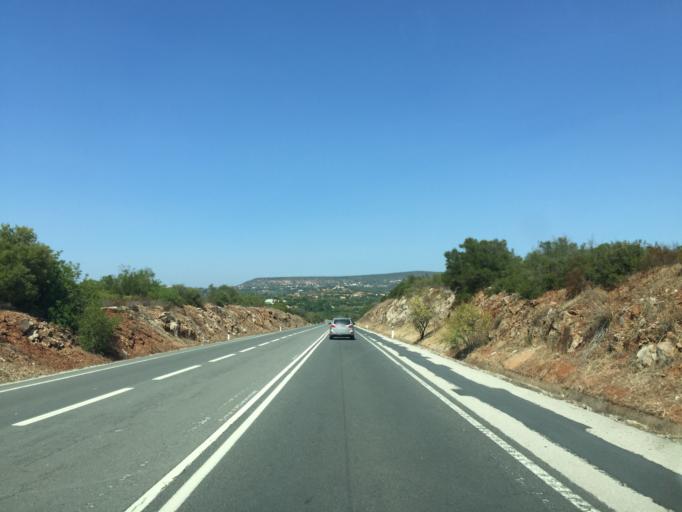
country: PT
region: Faro
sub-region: Silves
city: Sao Bartolomeu de Messines
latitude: 37.2028
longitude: -8.2599
